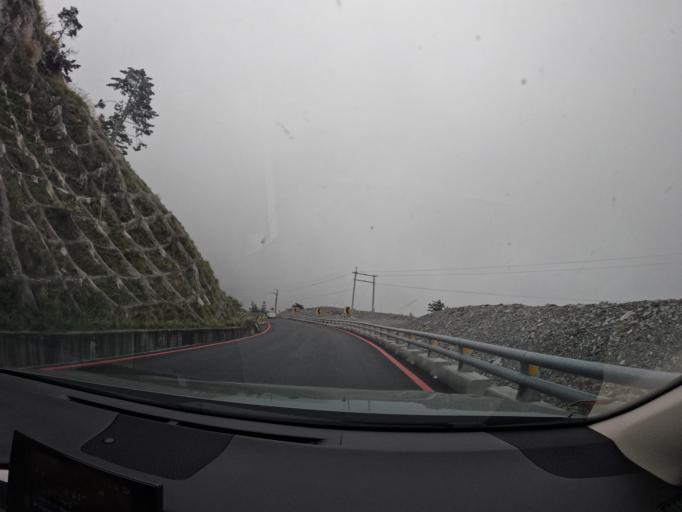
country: TW
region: Taiwan
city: Lugu
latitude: 23.2670
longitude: 120.9694
